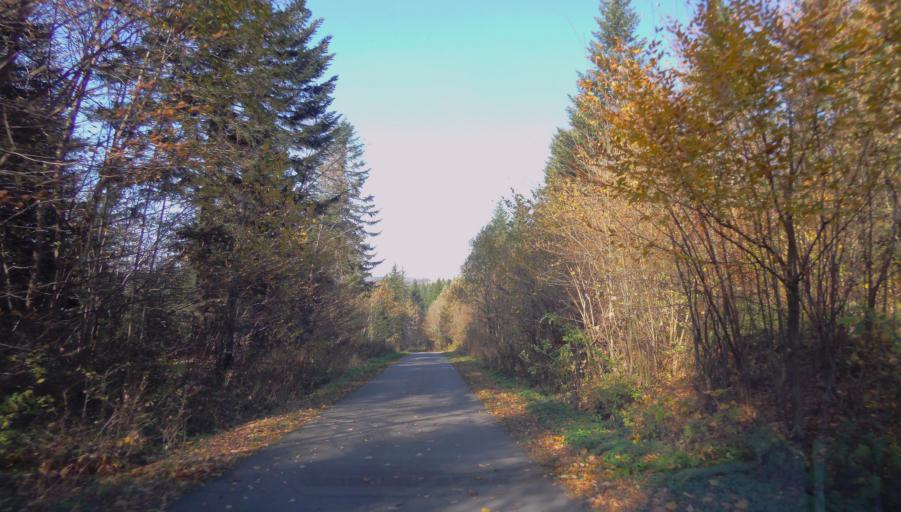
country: PL
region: Subcarpathian Voivodeship
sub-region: Powiat leski
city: Polanczyk
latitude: 49.3208
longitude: 22.4378
